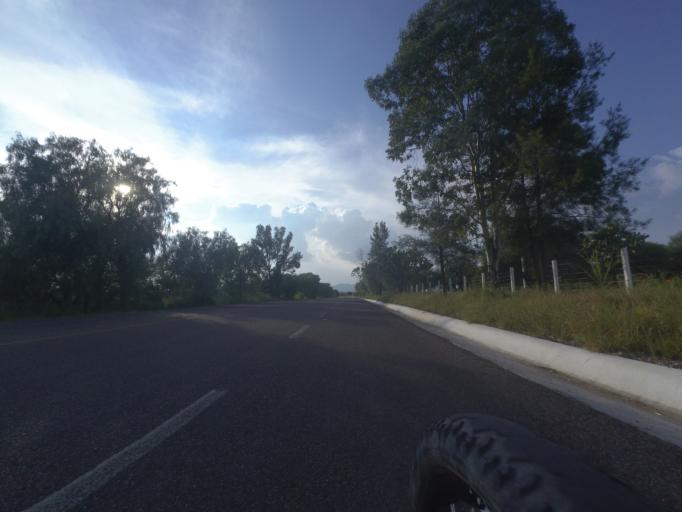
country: MX
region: Aguascalientes
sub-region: Aguascalientes
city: Penuelas (El Cienegal)
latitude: 21.7645
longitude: -102.3527
